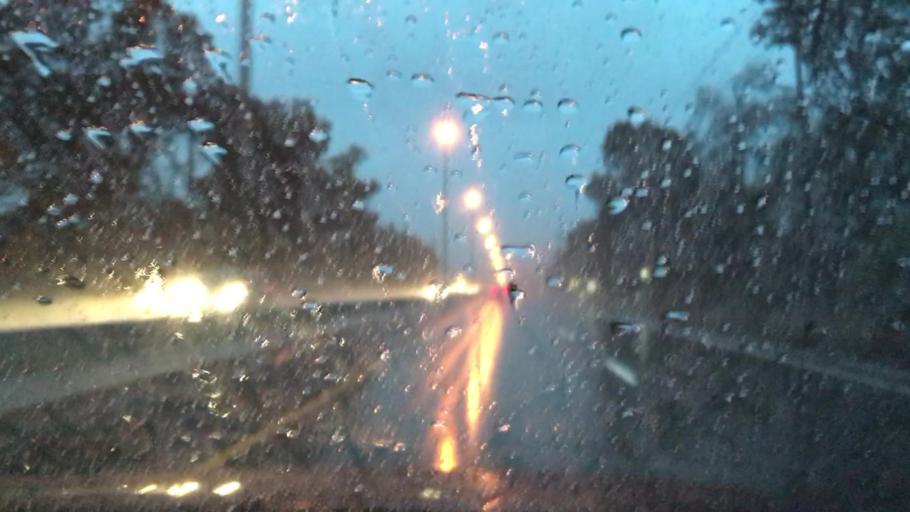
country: US
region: New Jersey
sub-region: Bergen County
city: Fair Lawn
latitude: 40.9324
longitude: -74.1134
